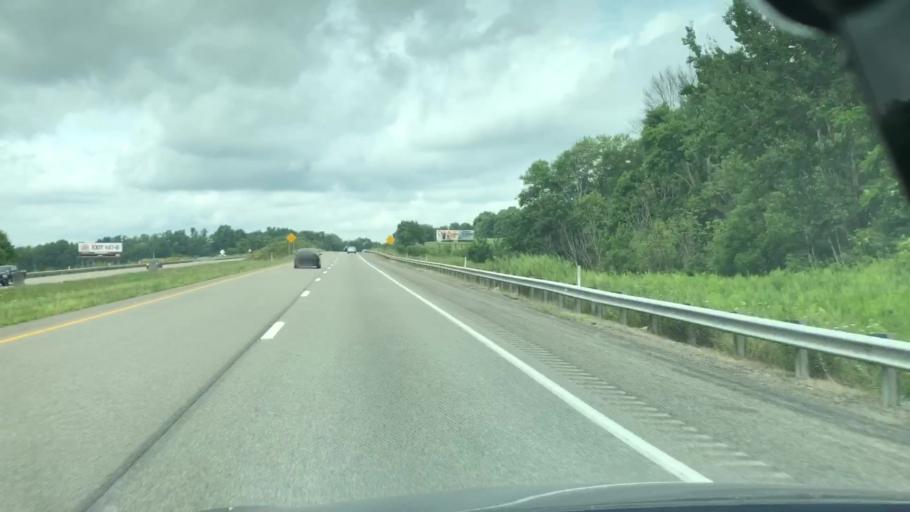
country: US
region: Pennsylvania
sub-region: Crawford County
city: Meadville
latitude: 41.5654
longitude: -80.1820
